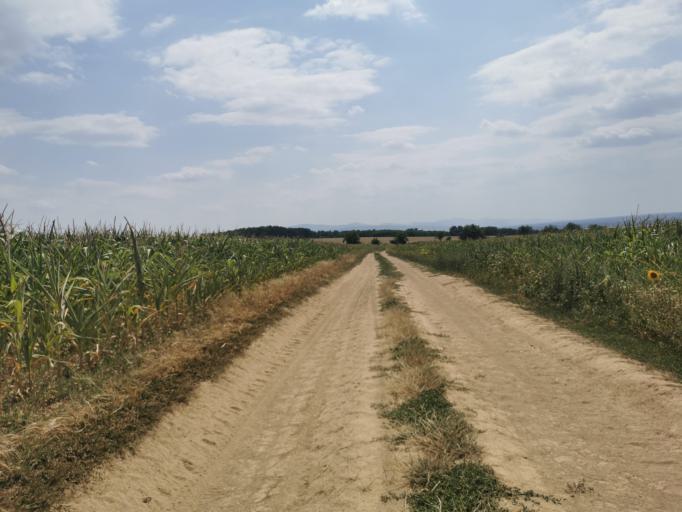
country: SK
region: Trnavsky
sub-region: Okres Senica
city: Senica
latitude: 48.6806
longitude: 17.4263
